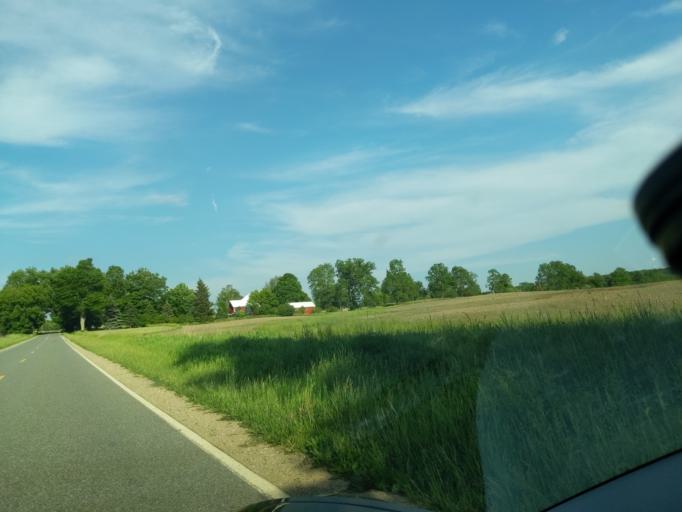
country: US
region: Michigan
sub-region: Barry County
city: Nashville
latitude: 42.6251
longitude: -85.1093
